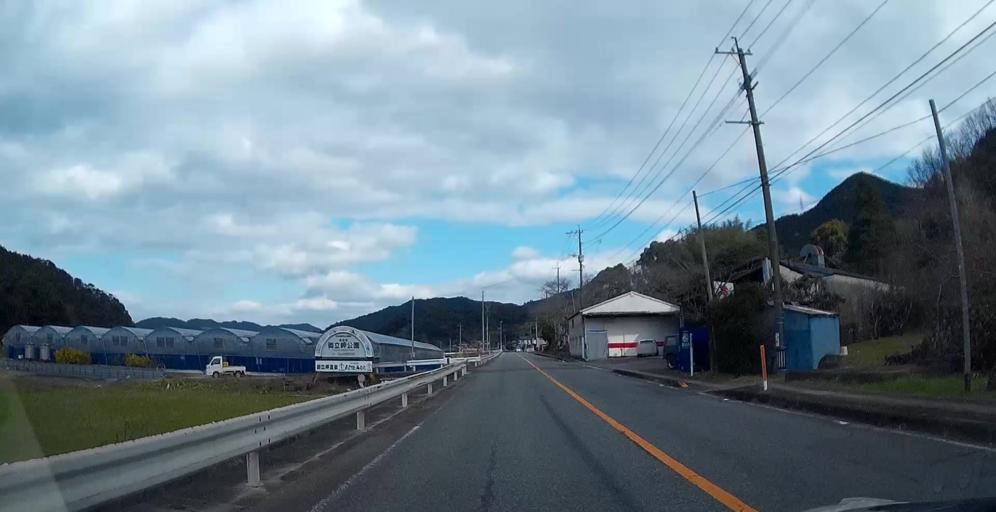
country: JP
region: Kumamoto
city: Minamata
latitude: 32.3428
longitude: 130.4996
